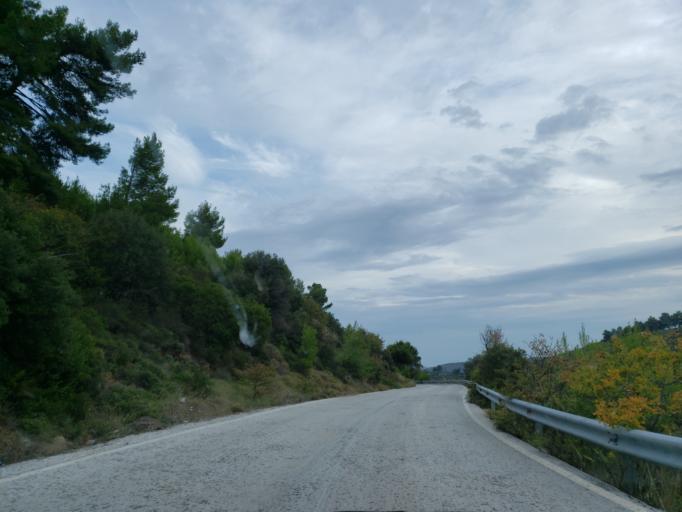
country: GR
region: Attica
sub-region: Nomarchia Anatolikis Attikis
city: Varnavas
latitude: 38.2127
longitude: 23.9428
